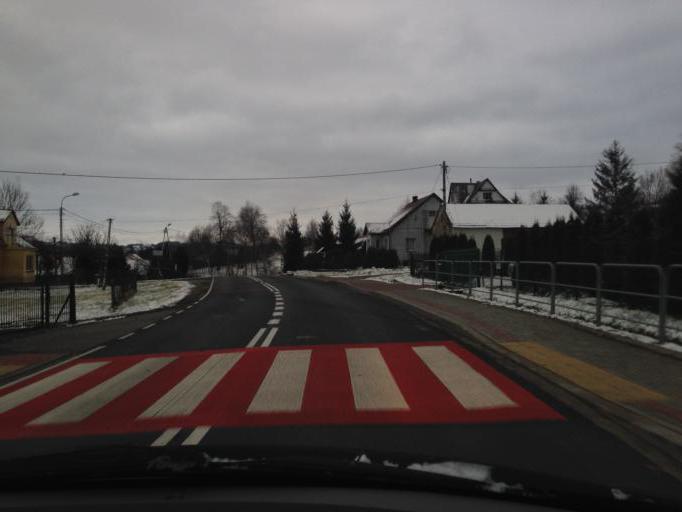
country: PL
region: Lesser Poland Voivodeship
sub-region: Powiat tarnowski
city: Gromnik
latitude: 49.8355
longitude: 20.9880
